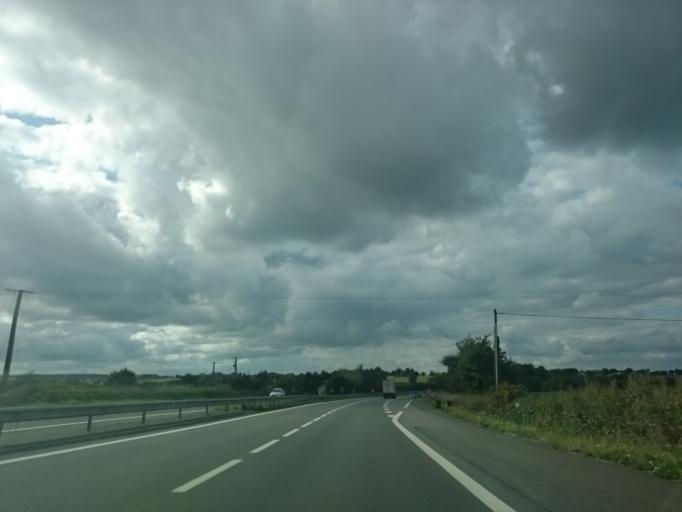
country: FR
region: Brittany
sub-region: Departement d'Ille-et-Vilaine
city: Quedillac
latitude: 48.2200
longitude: -2.1075
